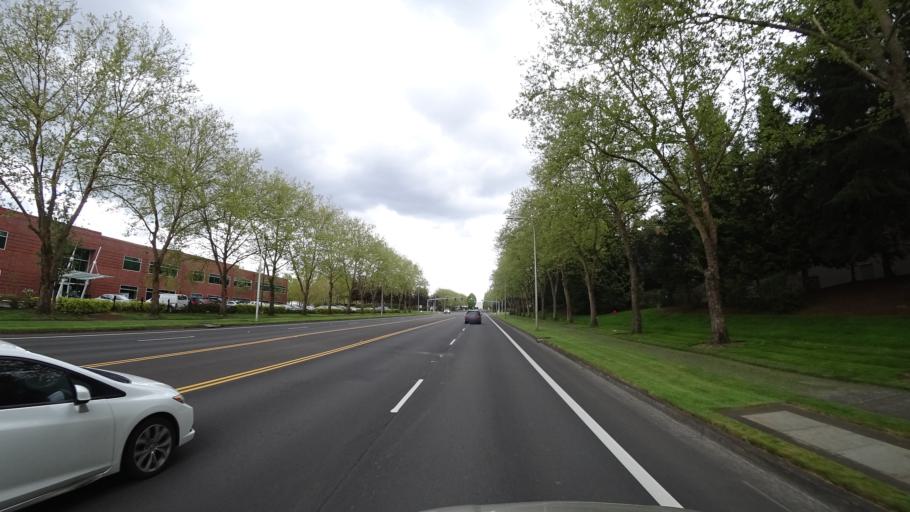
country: US
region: Oregon
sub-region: Washington County
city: Rockcreek
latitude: 45.5458
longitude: -122.8889
